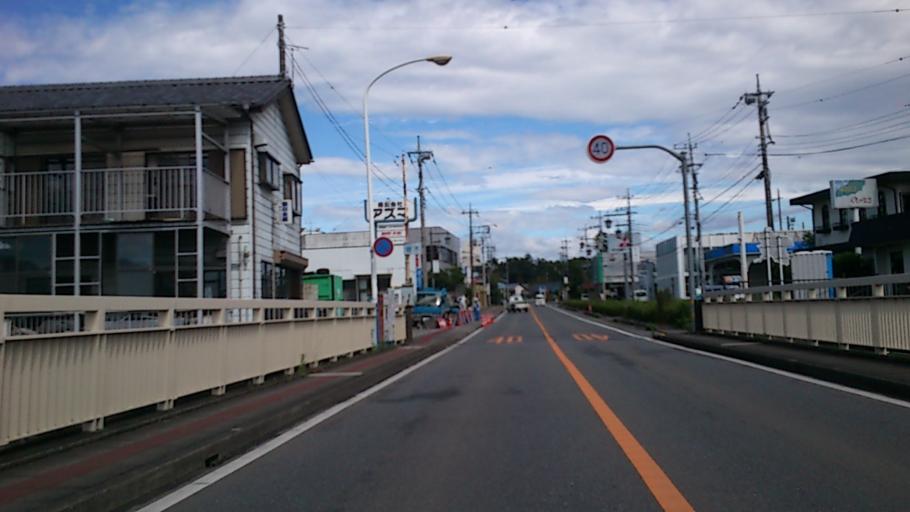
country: JP
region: Gunma
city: Tomioka
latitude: 36.2579
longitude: 138.9157
